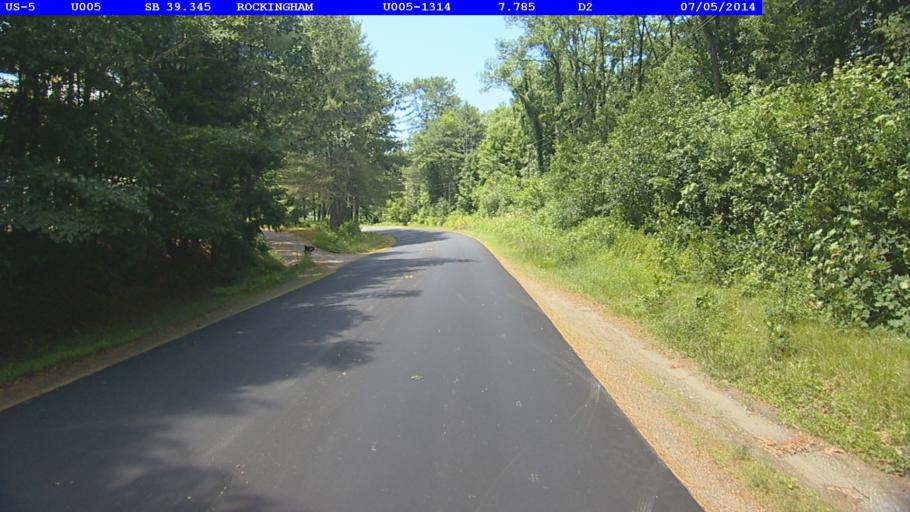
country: US
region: New Hampshire
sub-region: Sullivan County
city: Charlestown
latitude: 43.2235
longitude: -72.4478
